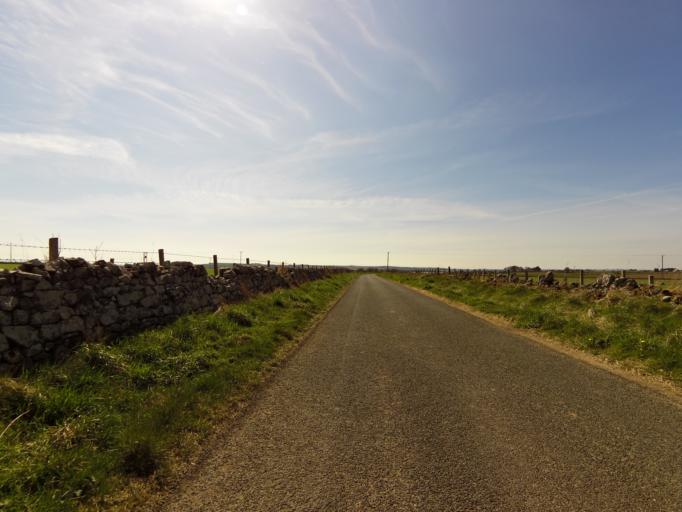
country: GB
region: Scotland
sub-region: Angus
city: Montrose
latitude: 56.6715
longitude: -2.4991
